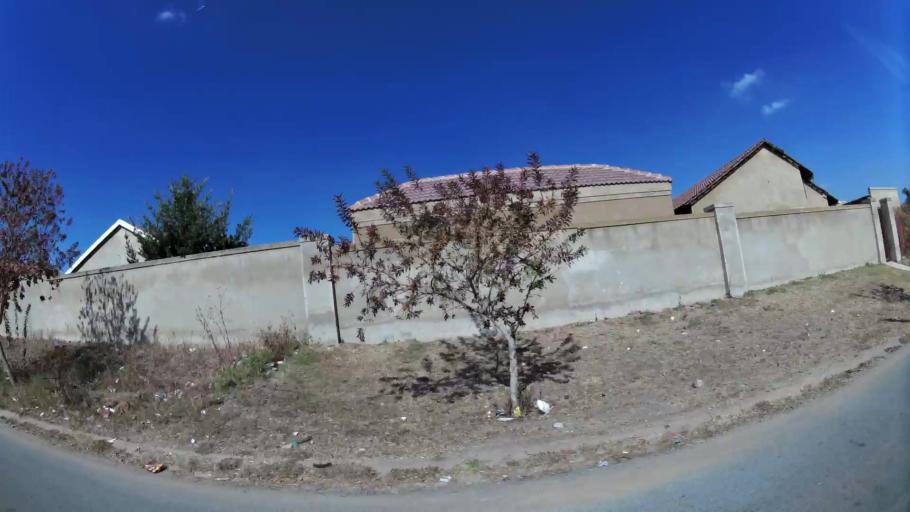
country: ZA
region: Gauteng
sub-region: West Rand District Municipality
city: Muldersdriseloop
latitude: -26.0161
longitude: 27.9340
